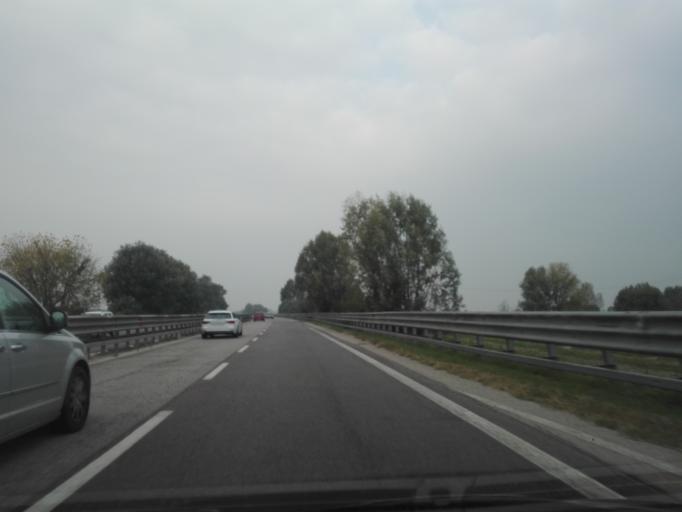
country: IT
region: Veneto
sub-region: Provincia di Verona
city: Villa Bartolomea
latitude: 45.1502
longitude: 11.3402
